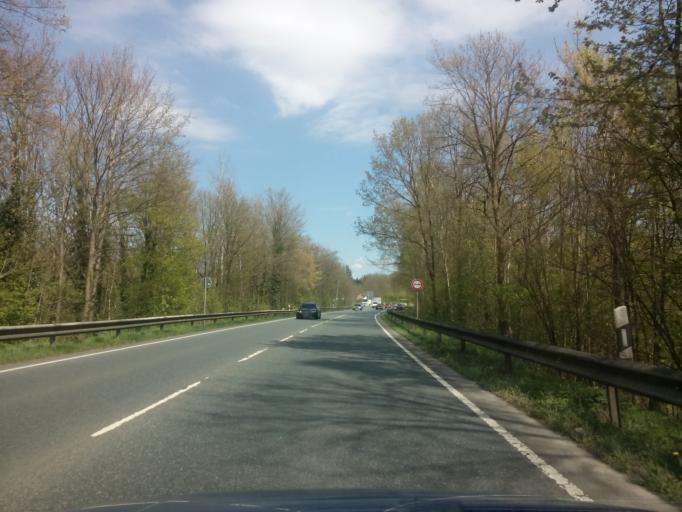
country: DE
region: Lower Saxony
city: Osterholz-Scharmbeck
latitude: 53.2361
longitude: 8.7785
